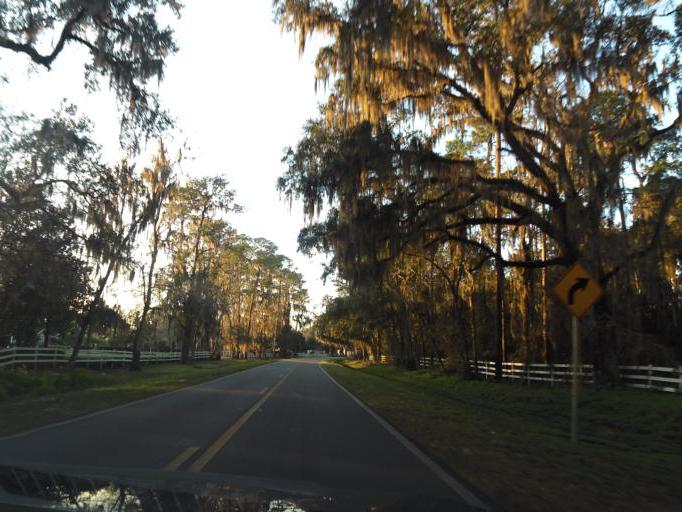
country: US
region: Florida
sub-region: Clay County
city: Green Cove Springs
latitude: 29.9019
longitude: -81.5862
